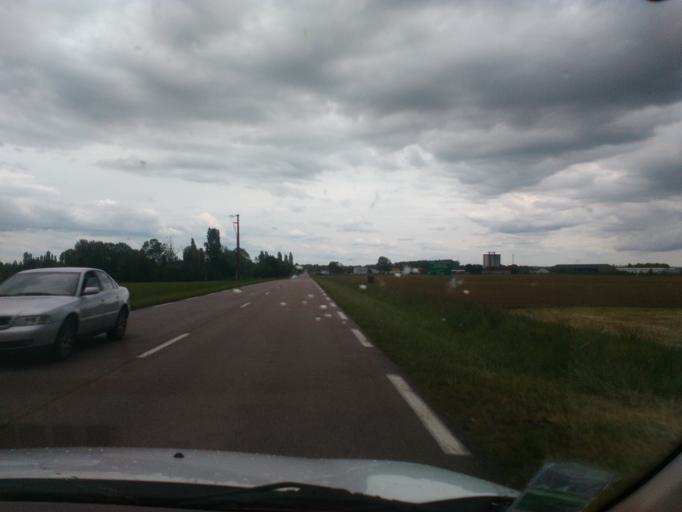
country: FR
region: Champagne-Ardenne
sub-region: Departement de l'Aube
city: Lusigny-sur-Barse
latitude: 48.2466
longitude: 4.2724
